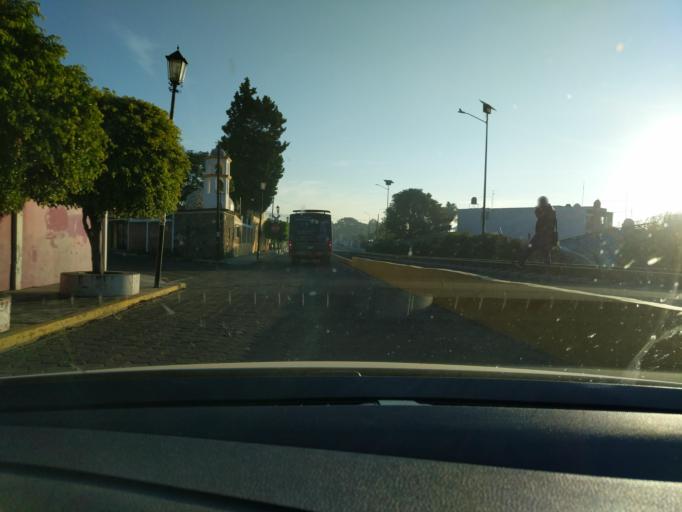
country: MX
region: Puebla
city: Cholula
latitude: 19.0610
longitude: -98.3005
